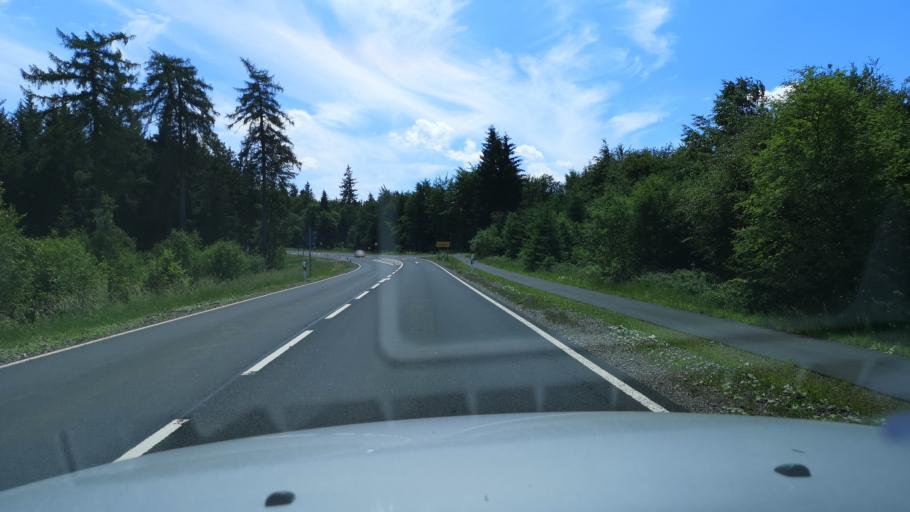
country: DE
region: Bavaria
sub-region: Upper Franconia
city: Ludwigsstadt
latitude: 50.4522
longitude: 11.3511
